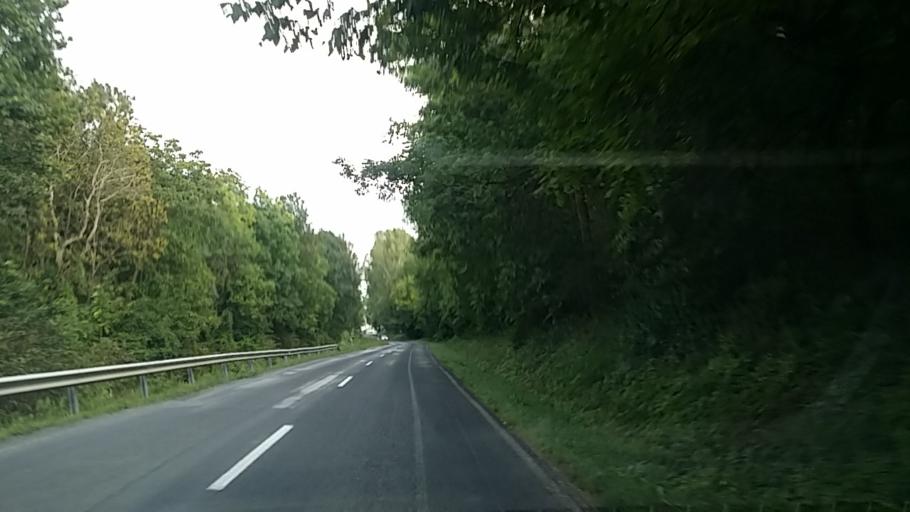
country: HU
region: Gyor-Moson-Sopron
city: Nagycenk
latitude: 47.6296
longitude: 16.7346
